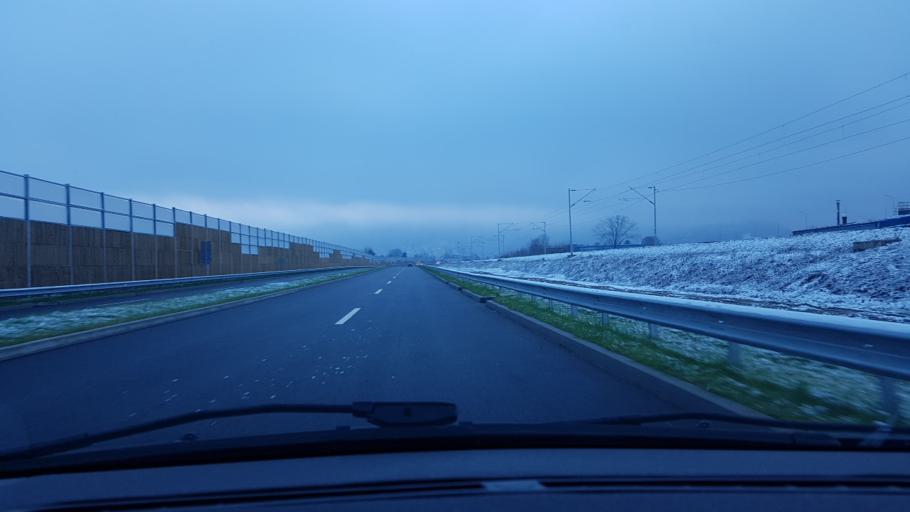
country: HR
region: Zagrebacka
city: Zapresic
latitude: 45.8538
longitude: 15.7994
